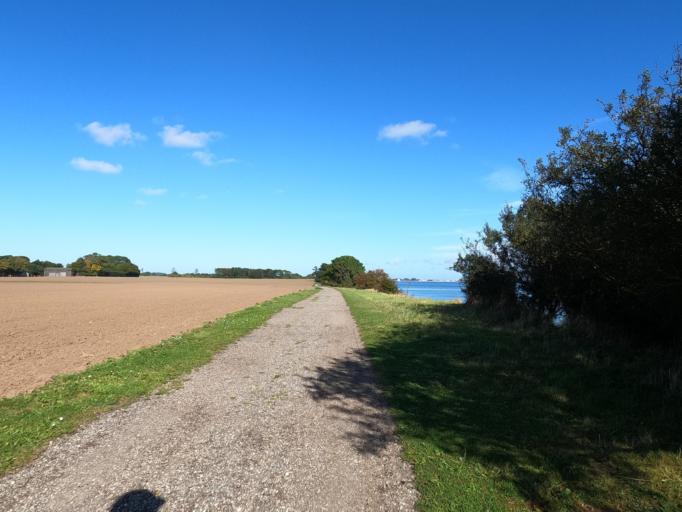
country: DE
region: Schleswig-Holstein
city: Neukirchen
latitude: 54.3099
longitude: 11.0745
